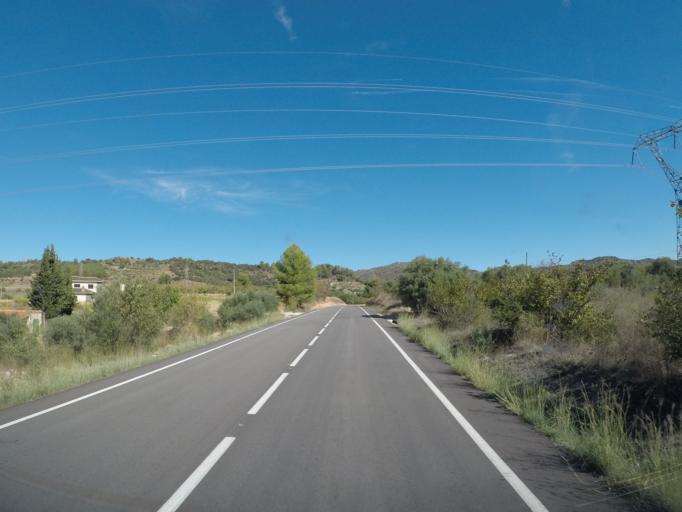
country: ES
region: Catalonia
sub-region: Provincia de Tarragona
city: Falset
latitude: 41.1578
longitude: 0.8145
